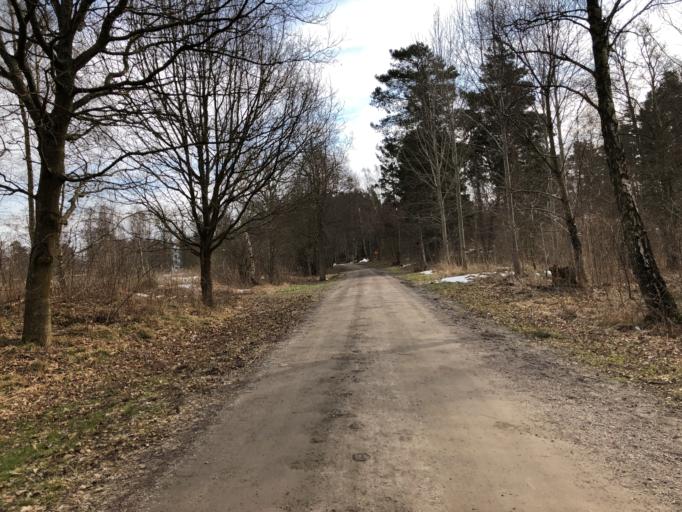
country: SE
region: Kalmar
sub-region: Kalmar Kommun
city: Kalmar
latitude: 56.6568
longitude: 16.3210
